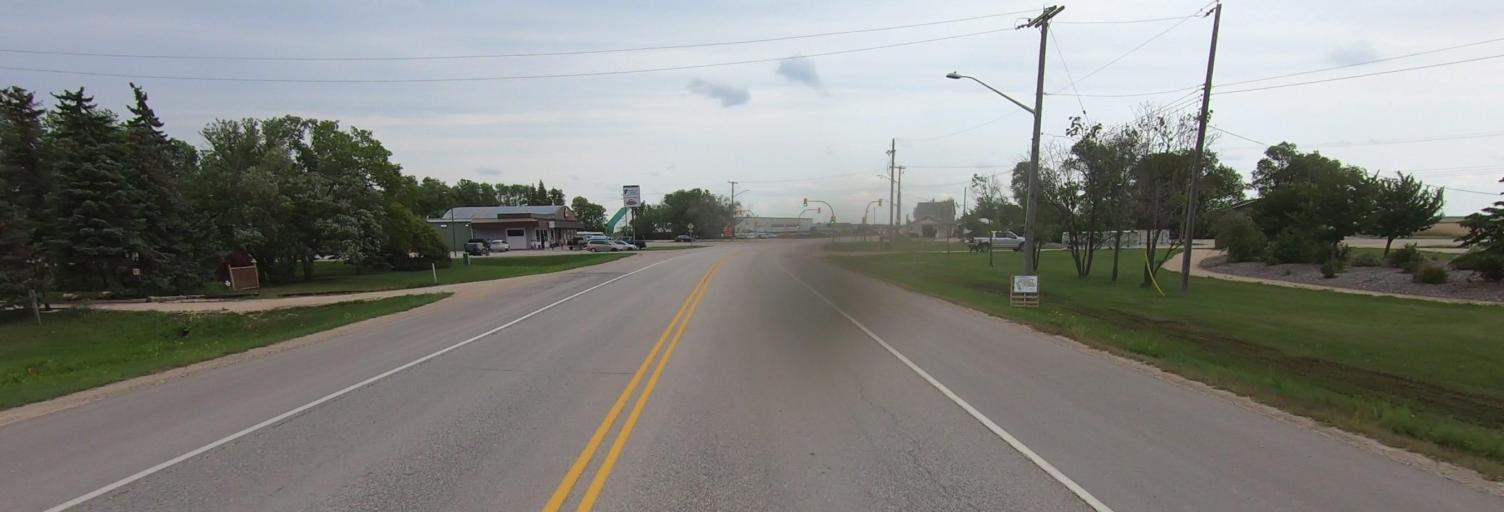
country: CA
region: Manitoba
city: Headingley
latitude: 49.7727
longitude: -97.3238
